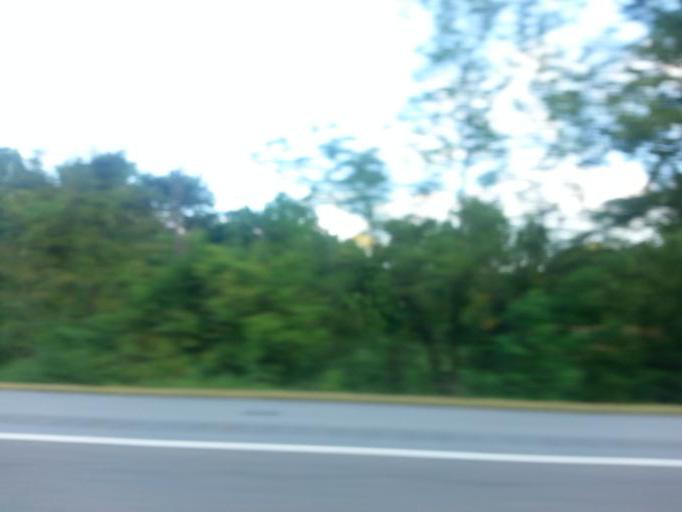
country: US
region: Tennessee
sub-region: Grainger County
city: Blaine
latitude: 36.1261
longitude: -83.7211
